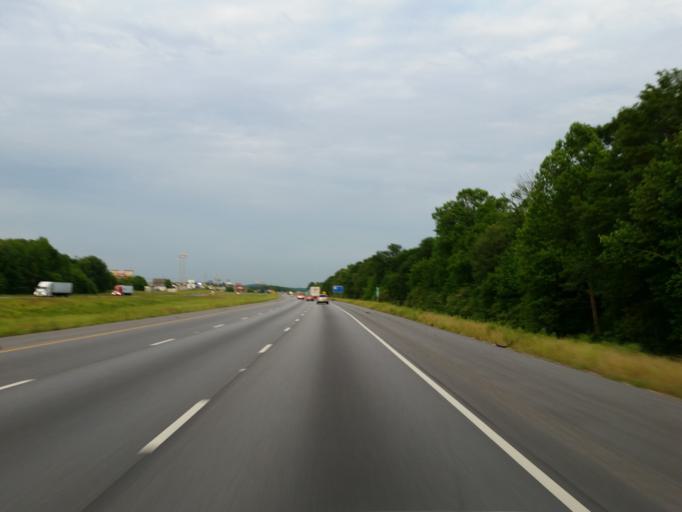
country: US
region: Alabama
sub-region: Calhoun County
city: Oxford
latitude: 33.6065
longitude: -85.8065
